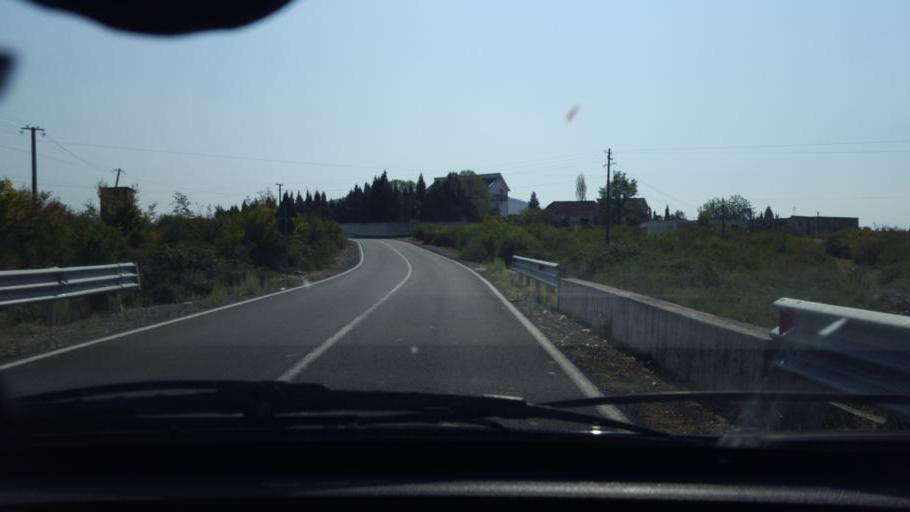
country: AL
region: Shkoder
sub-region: Rrethi i Malesia e Madhe
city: Hot
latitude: 42.3385
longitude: 19.4351
